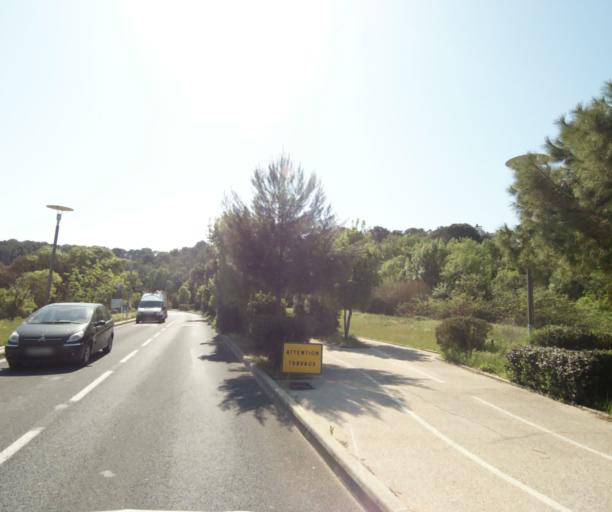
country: FR
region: Languedoc-Roussillon
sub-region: Departement de l'Herault
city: Montferrier-sur-Lez
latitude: 43.6447
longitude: 3.8626
